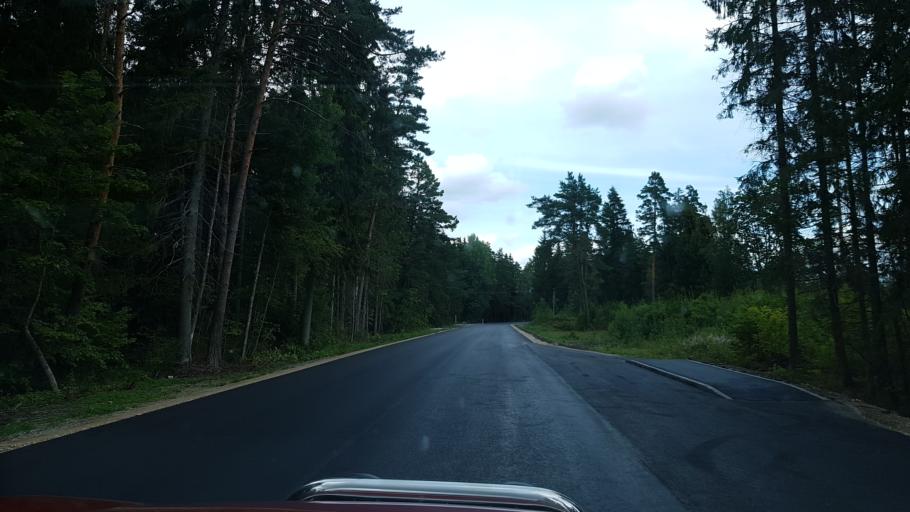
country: EE
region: Harju
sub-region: Nissi vald
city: Turba
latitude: 59.0968
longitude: 24.0007
